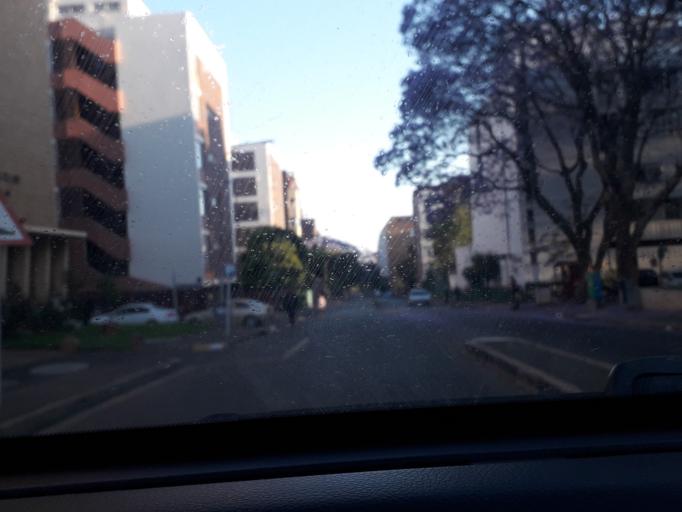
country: ZA
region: Gauteng
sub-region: City of Johannesburg Metropolitan Municipality
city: Johannesburg
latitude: -26.1687
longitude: 28.0492
